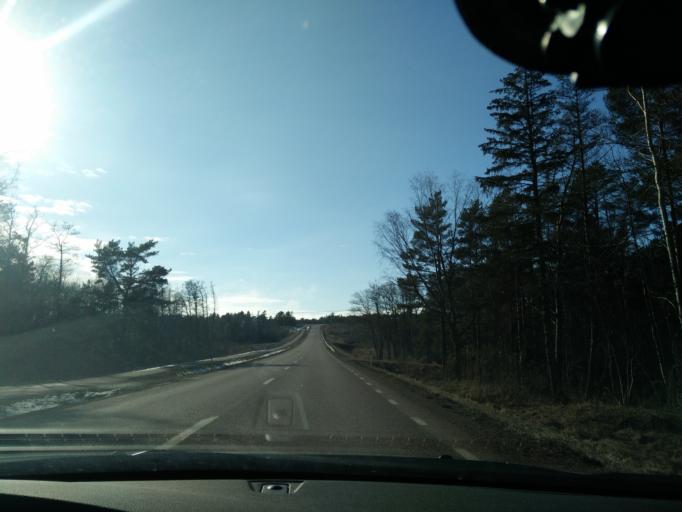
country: AX
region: Alands landsbygd
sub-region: Eckeroe
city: Eckeroe
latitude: 60.2149
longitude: 19.6653
